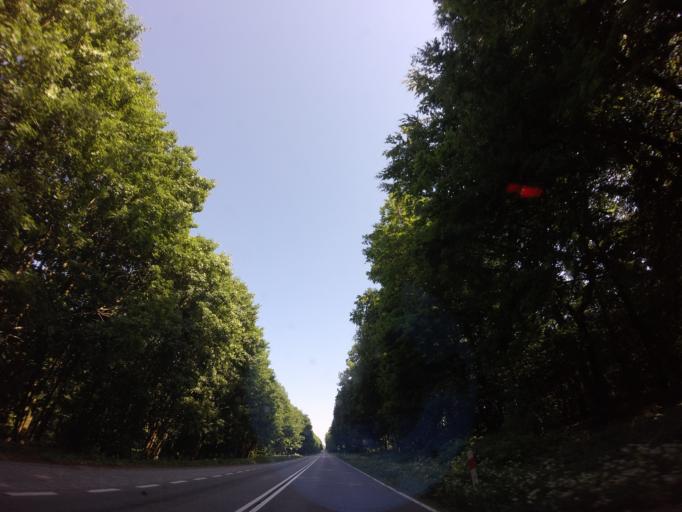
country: PL
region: West Pomeranian Voivodeship
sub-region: Powiat gryfinski
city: Stare Czarnowo
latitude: 53.3353
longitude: 14.7695
